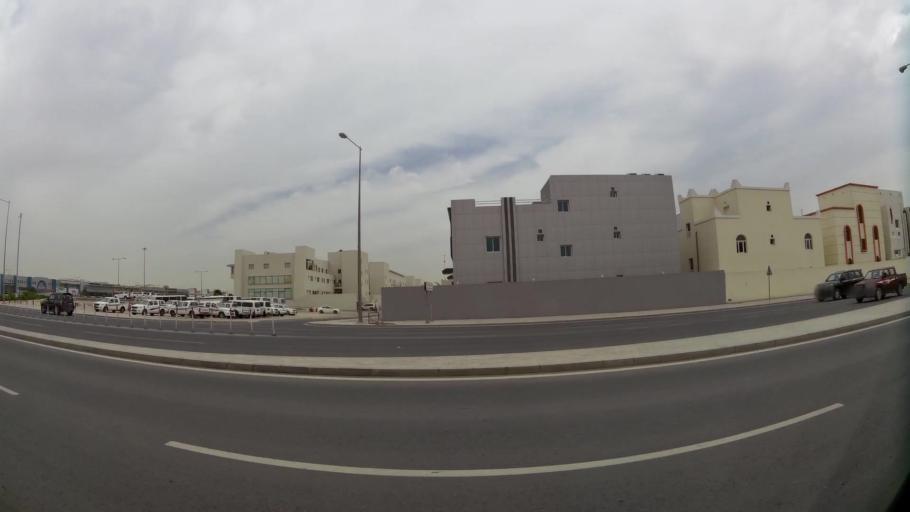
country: QA
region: Baladiyat ar Rayyan
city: Ar Rayyan
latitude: 25.2431
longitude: 51.4642
